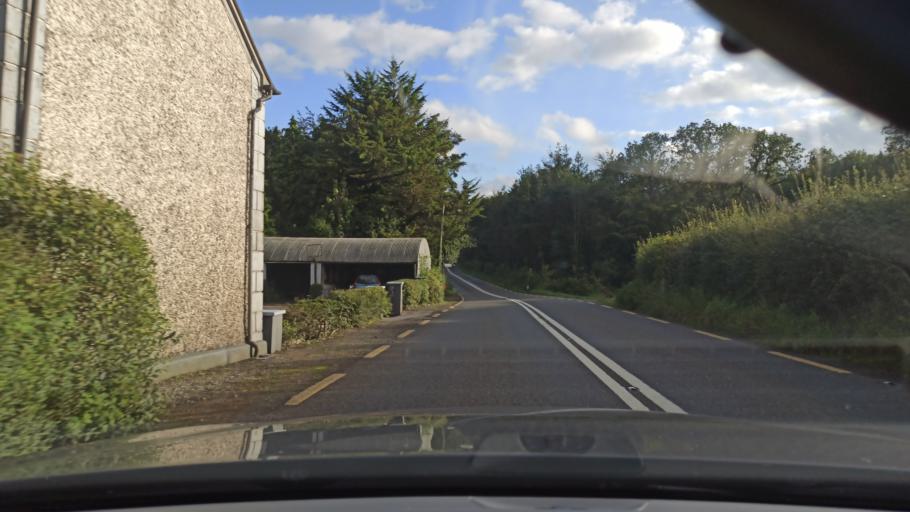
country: IE
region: Munster
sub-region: North Tipperary
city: Roscrea
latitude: 52.9074
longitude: -7.7955
